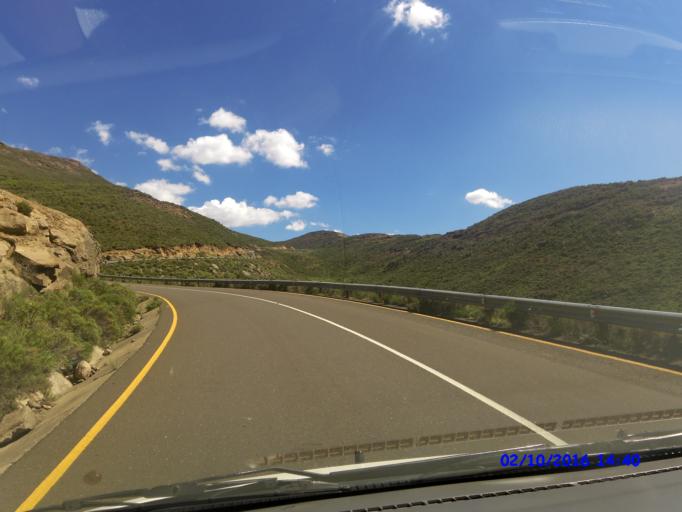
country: LS
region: Maseru
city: Nako
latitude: -29.5237
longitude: 28.0611
